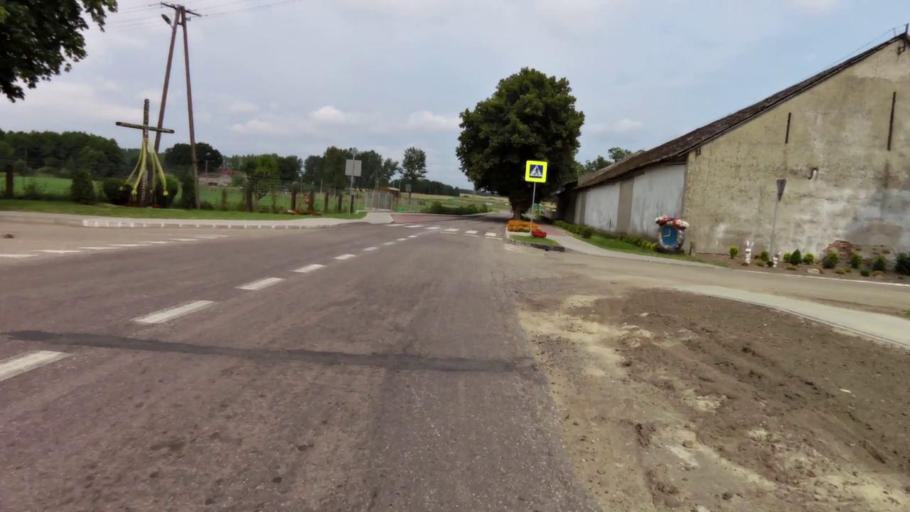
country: PL
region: West Pomeranian Voivodeship
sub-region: Powiat drawski
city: Drawsko Pomorskie
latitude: 53.5693
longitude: 15.8454
